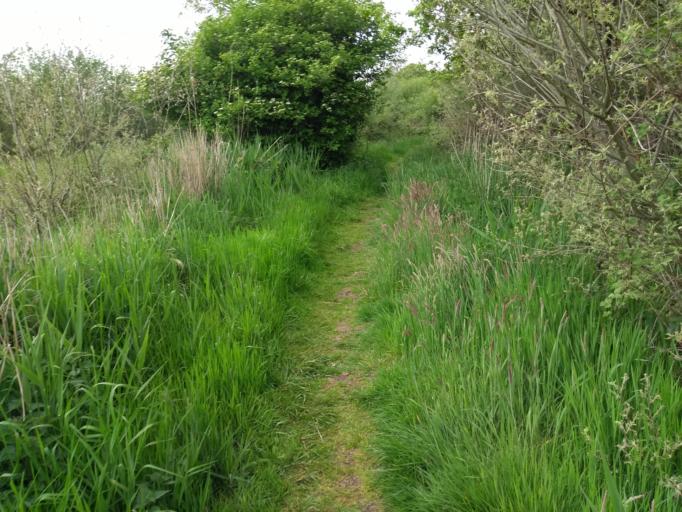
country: NL
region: Overijssel
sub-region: Gemeente Twenterand
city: Vriezenveen
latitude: 52.4104
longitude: 6.6649
